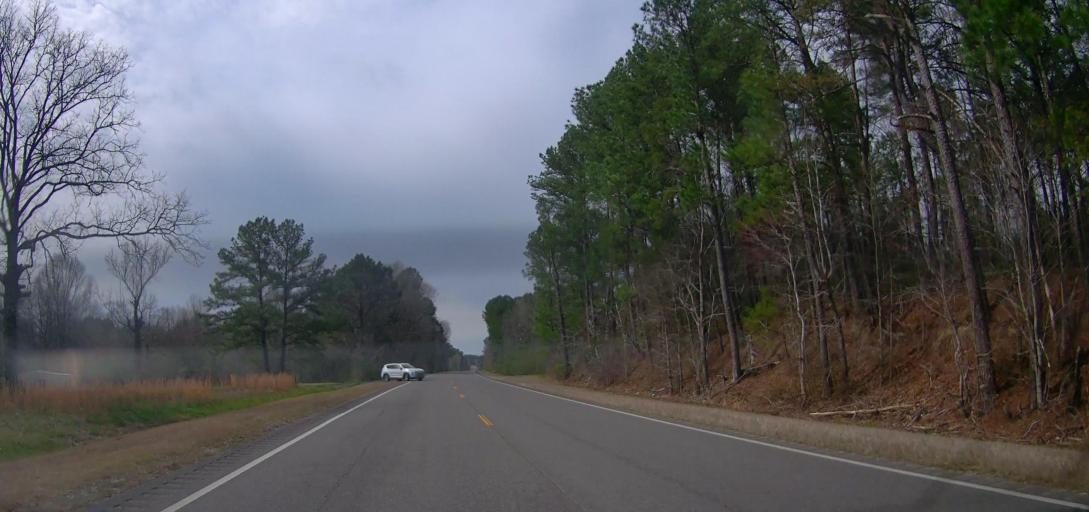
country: US
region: Alabama
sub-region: Walker County
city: Carbon Hill
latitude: 33.9026
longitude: -87.5480
